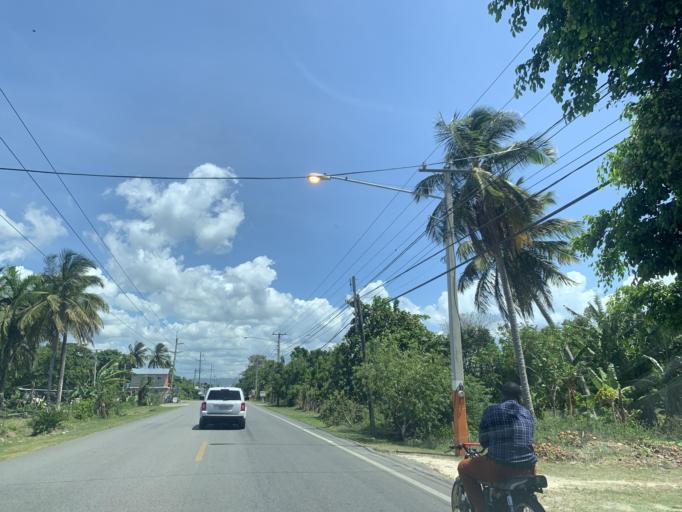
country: DO
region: Puerto Plata
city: Cabarete
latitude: 19.7225
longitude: -70.3870
